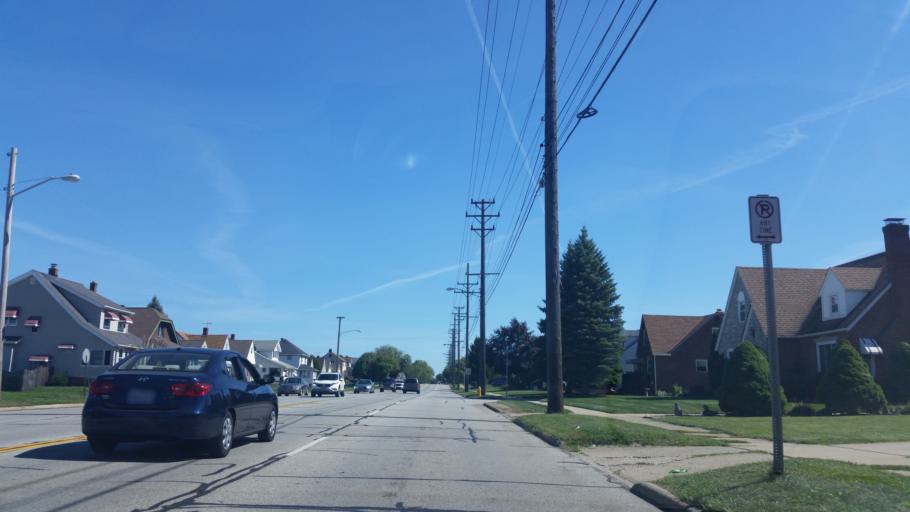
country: US
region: Ohio
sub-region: Cuyahoga County
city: Parma
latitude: 41.4048
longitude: -81.7311
